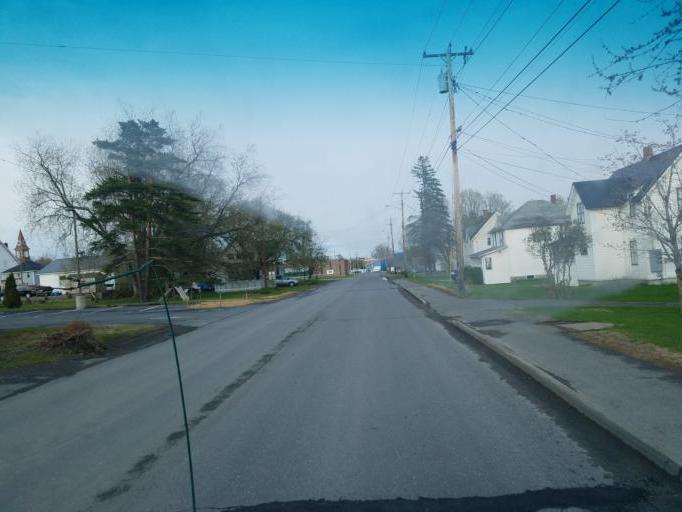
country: US
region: Maine
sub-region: Aroostook County
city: Caribou
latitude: 46.8585
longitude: -68.0192
